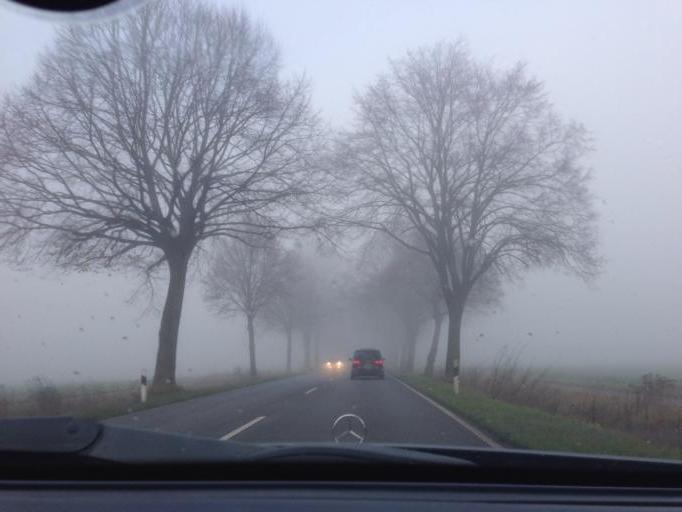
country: DE
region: Schleswig-Holstein
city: Stapelfeld
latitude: 53.6386
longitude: 10.1934
